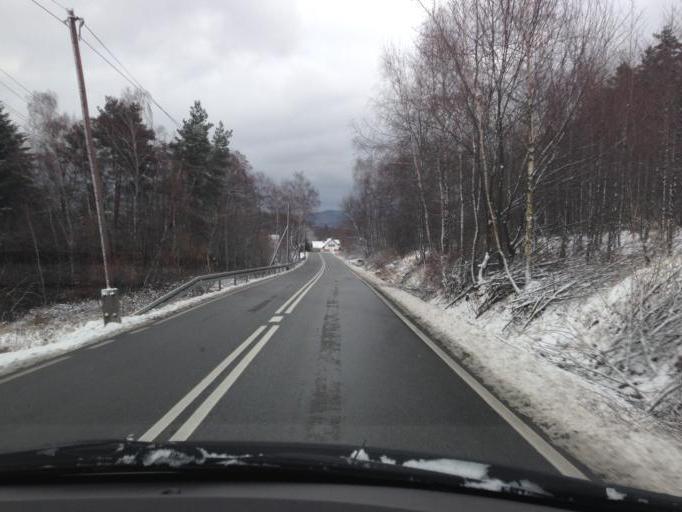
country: PL
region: Lesser Poland Voivodeship
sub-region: Powiat bochenski
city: Nowy Wisnicz
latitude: 49.8524
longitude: 20.4805
